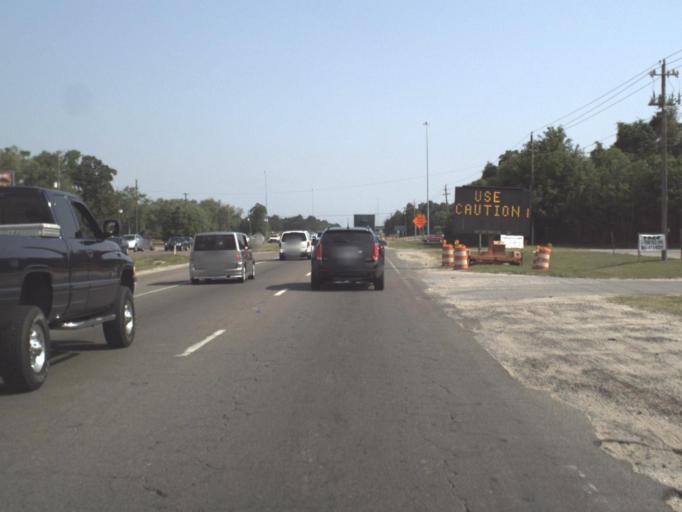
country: US
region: Florida
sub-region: Escambia County
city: Ensley
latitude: 30.5109
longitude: -87.2701
